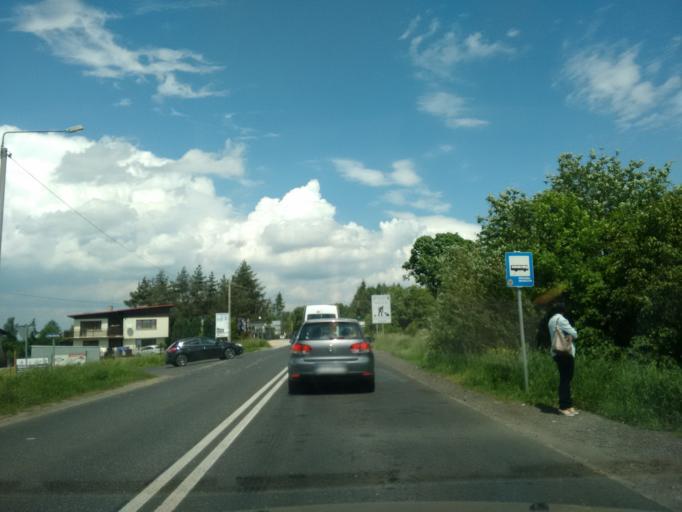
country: PL
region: Silesian Voivodeship
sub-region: Powiat cieszynski
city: Pruchna
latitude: 49.8631
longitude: 18.6807
